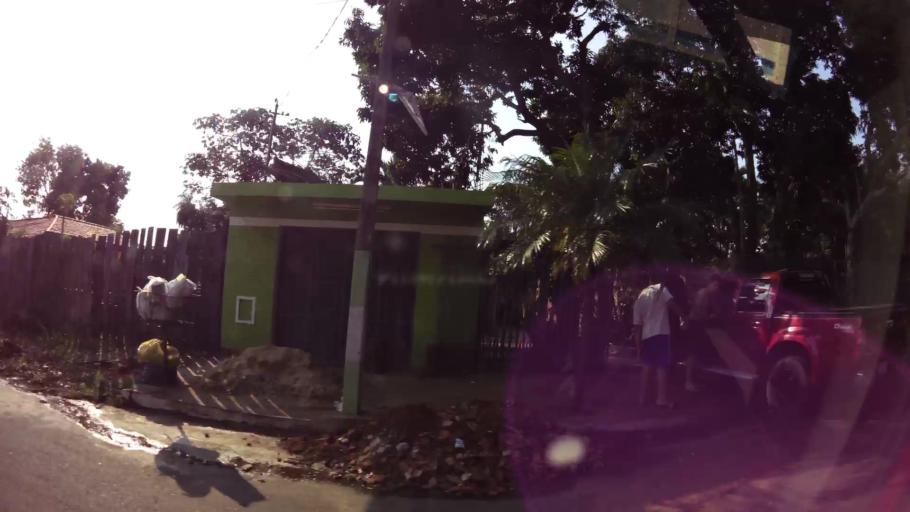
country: PY
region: Central
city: Lambare
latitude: -25.3433
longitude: -57.5860
